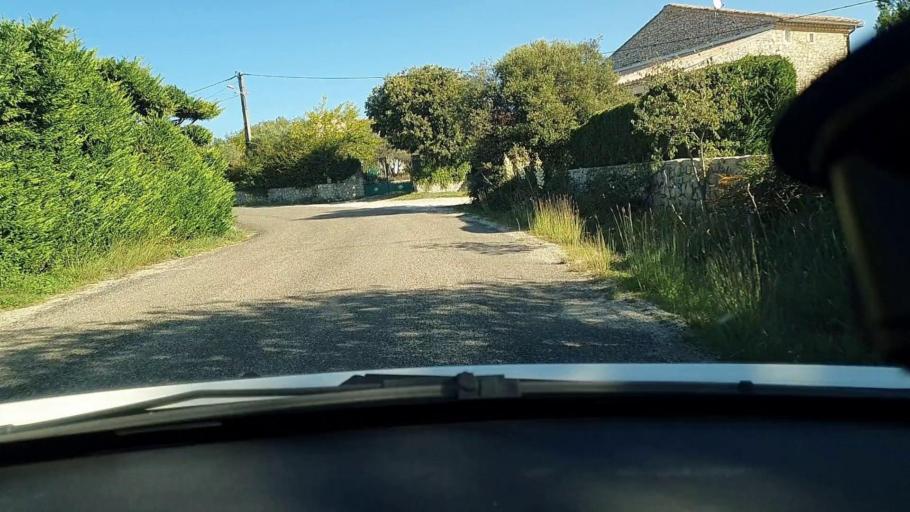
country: FR
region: Languedoc-Roussillon
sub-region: Departement du Gard
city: Barjac
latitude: 44.1866
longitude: 4.3258
